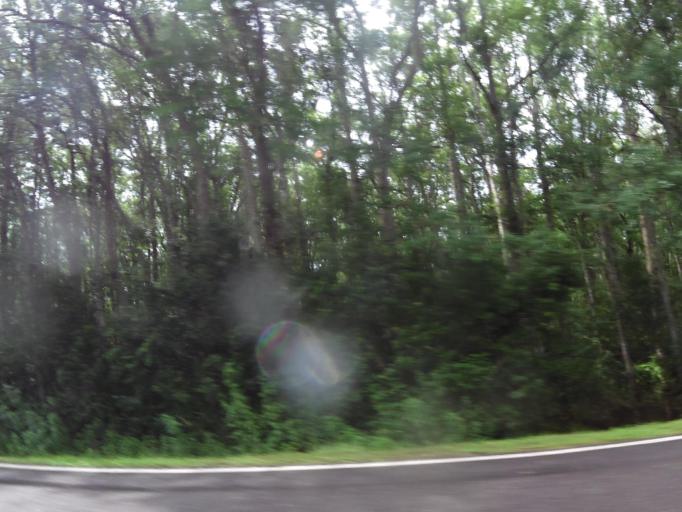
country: US
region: Florida
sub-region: Saint Johns County
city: Saint Augustine South
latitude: 29.8621
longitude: -81.3880
